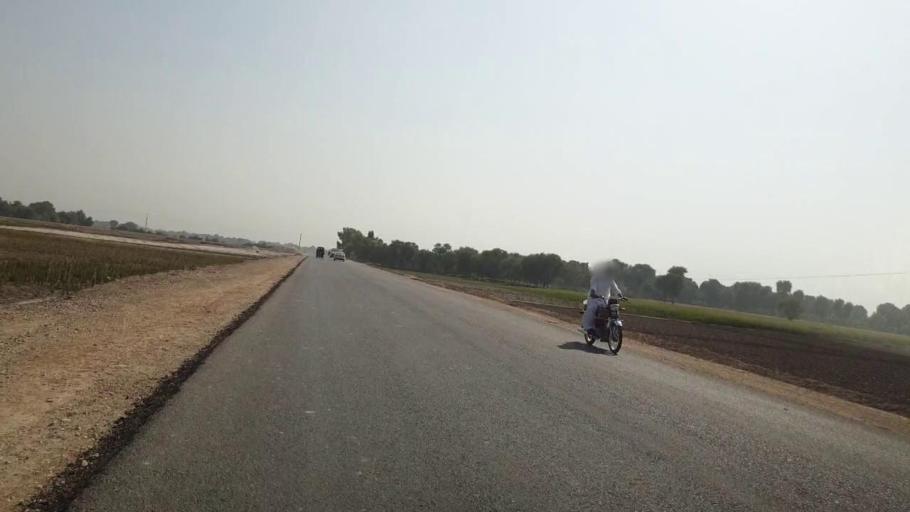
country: PK
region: Sindh
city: Dadu
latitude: 26.6517
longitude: 67.7763
